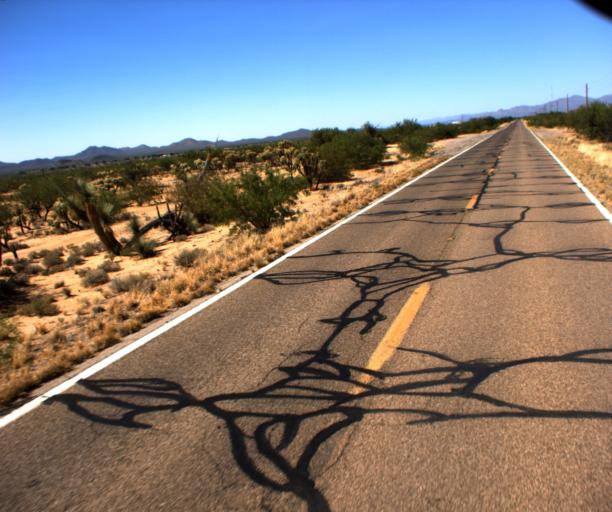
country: US
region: Arizona
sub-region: Pima County
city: Three Points
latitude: 32.0516
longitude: -111.3275
